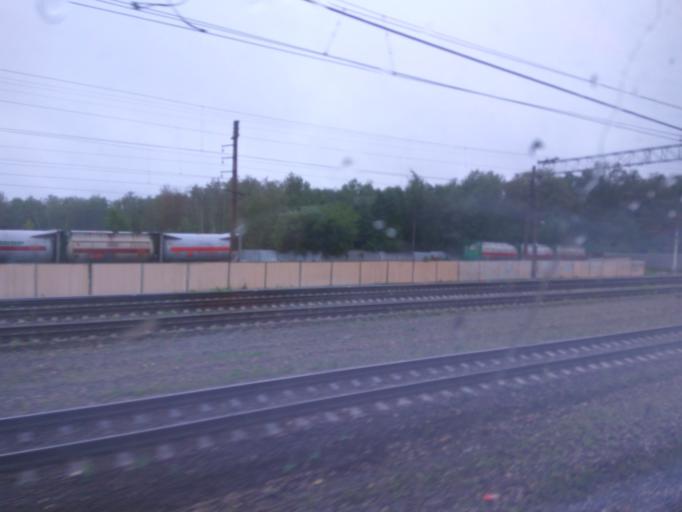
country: RU
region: Moskovskaya
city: Stupino
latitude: 54.9111
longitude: 38.0771
